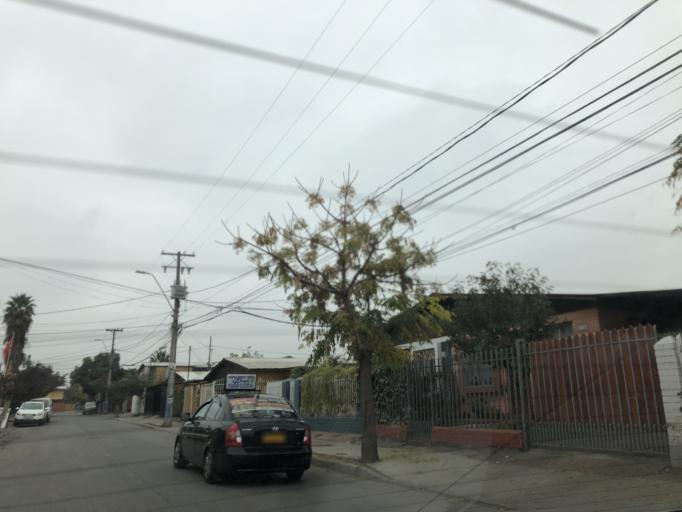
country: CL
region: Santiago Metropolitan
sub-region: Provincia de Cordillera
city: Puente Alto
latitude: -33.5909
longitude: -70.5883
